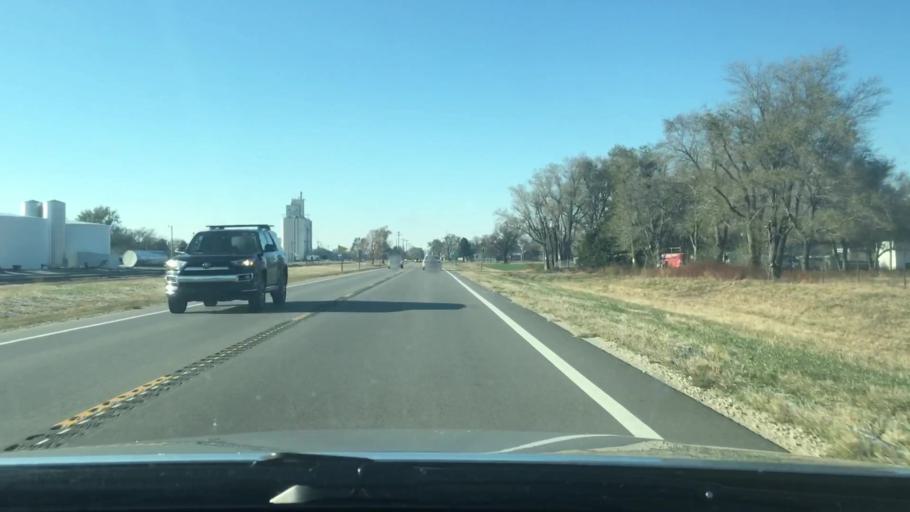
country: US
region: Kansas
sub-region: Reno County
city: Nickerson
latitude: 38.1425
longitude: -98.0766
